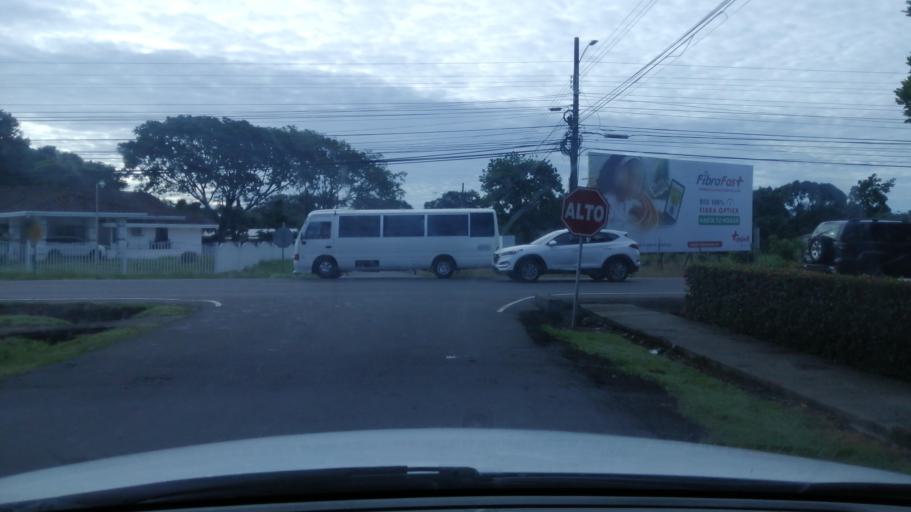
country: PA
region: Chiriqui
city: Mata del Nance
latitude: 8.4551
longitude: -82.4210
